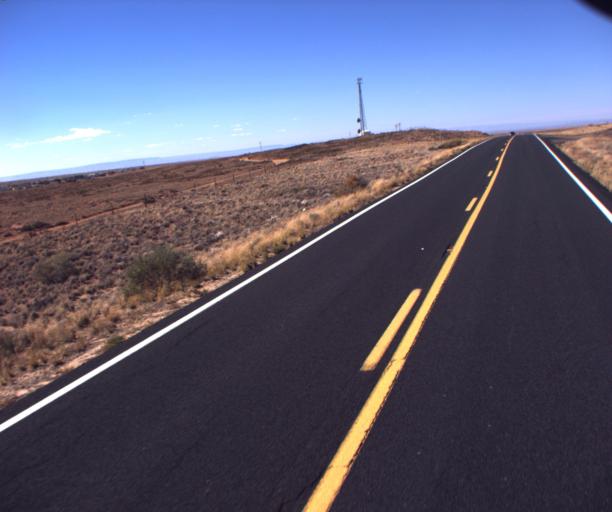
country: US
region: Arizona
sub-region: Coconino County
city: Tuba City
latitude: 35.9927
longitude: -111.0175
